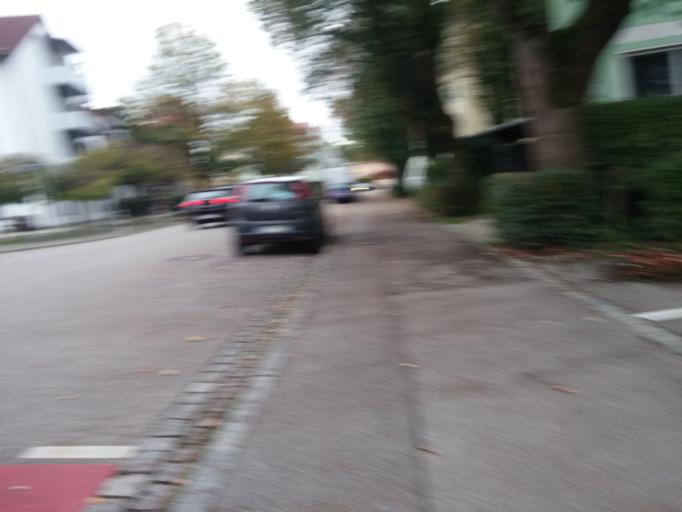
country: DE
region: Bavaria
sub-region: Upper Bavaria
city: Kirchseeon
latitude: 48.0735
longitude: 11.8856
